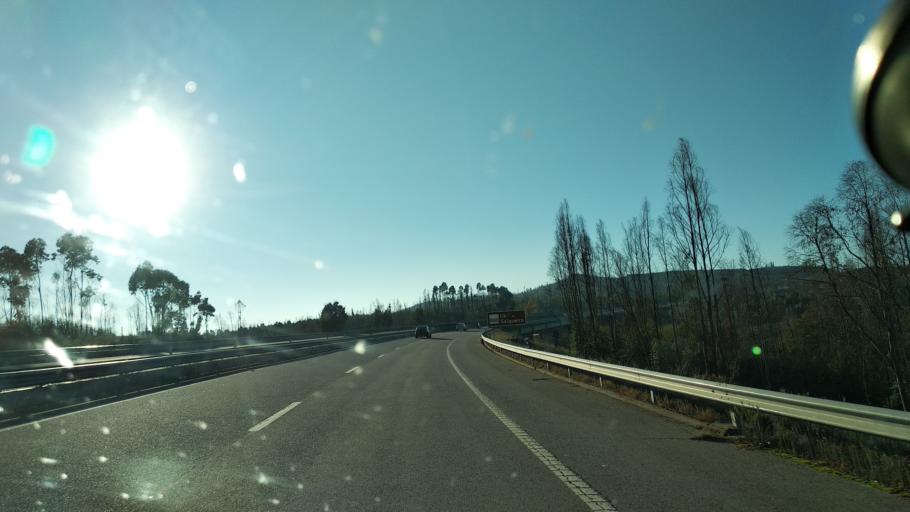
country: PT
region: Portalegre
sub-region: Gaviao
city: Gaviao
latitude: 39.5335
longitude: -7.8996
